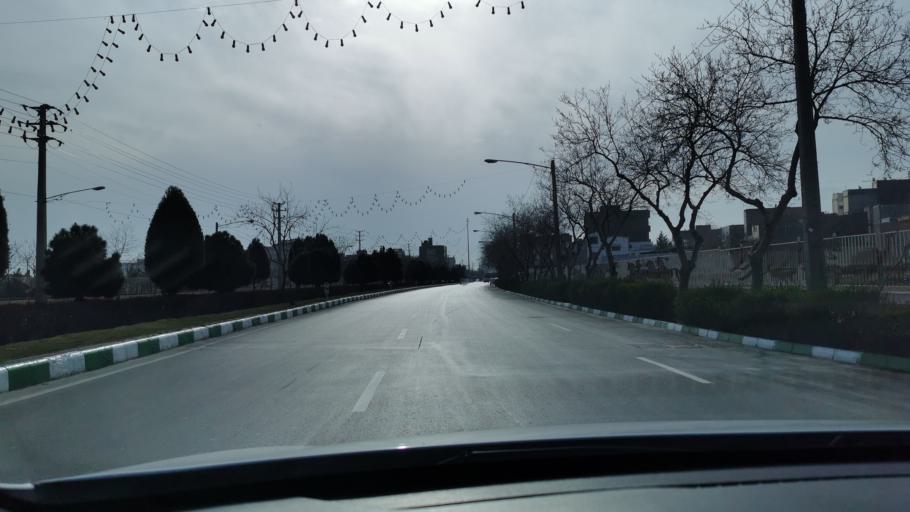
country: IR
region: Razavi Khorasan
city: Mashhad
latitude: 36.3001
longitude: 59.5220
